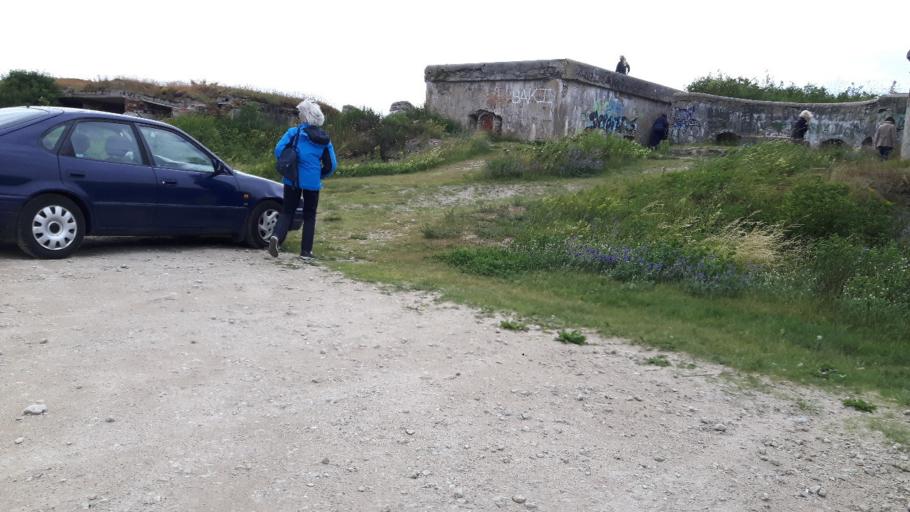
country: LV
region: Liepaja
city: Vec-Liepaja
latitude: 56.5915
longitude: 21.0159
